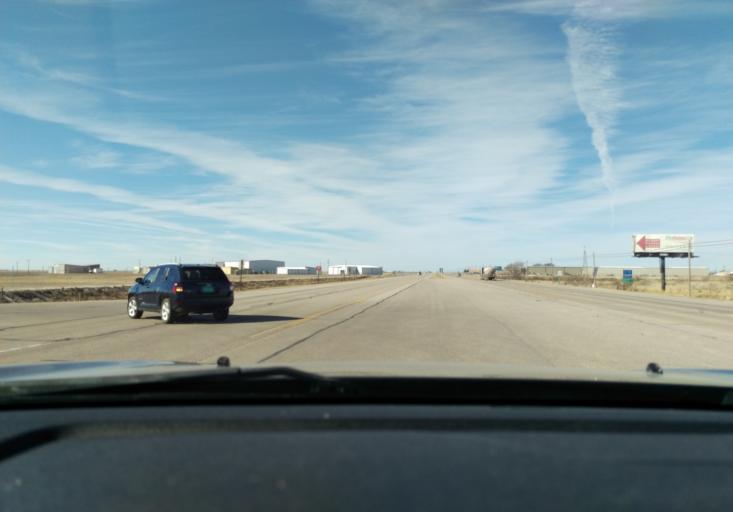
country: US
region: New Mexico
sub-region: Lea County
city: Hobbs
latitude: 32.6967
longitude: -103.2141
